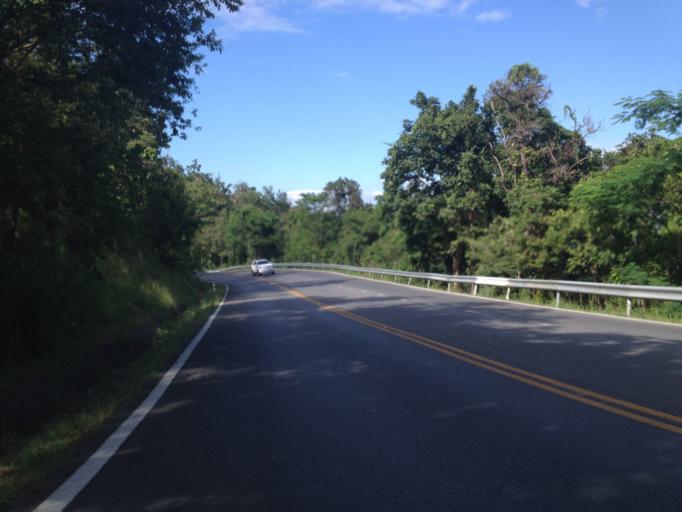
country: TH
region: Chiang Mai
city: Chiang Mai
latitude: 18.8132
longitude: 98.9427
